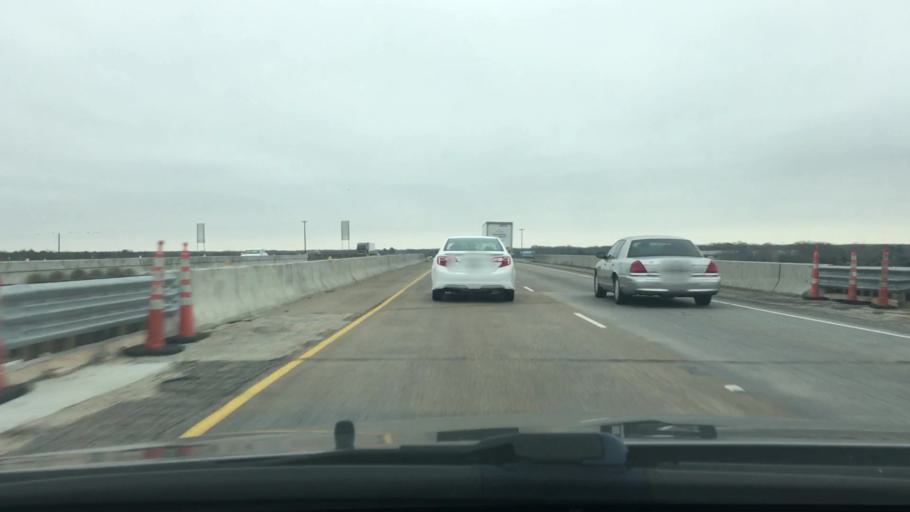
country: US
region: Texas
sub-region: Freestone County
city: Wortham
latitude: 31.8650
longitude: -96.3226
